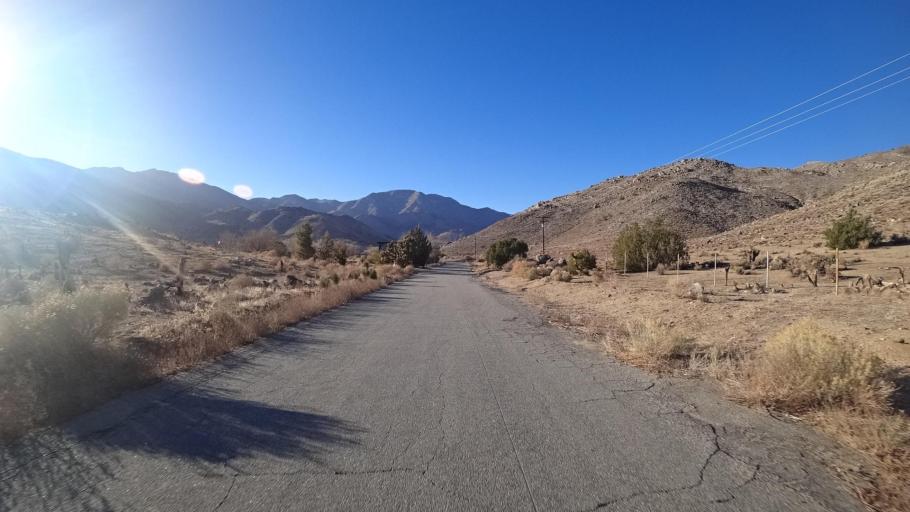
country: US
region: California
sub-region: Kern County
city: Weldon
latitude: 35.5635
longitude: -118.2411
